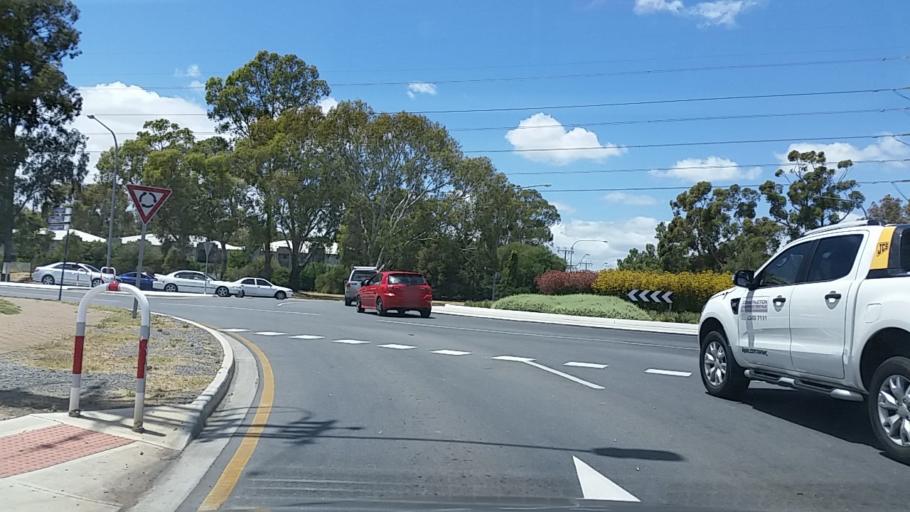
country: AU
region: South Australia
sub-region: Salisbury
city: Salisbury
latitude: -34.7727
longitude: 138.6158
